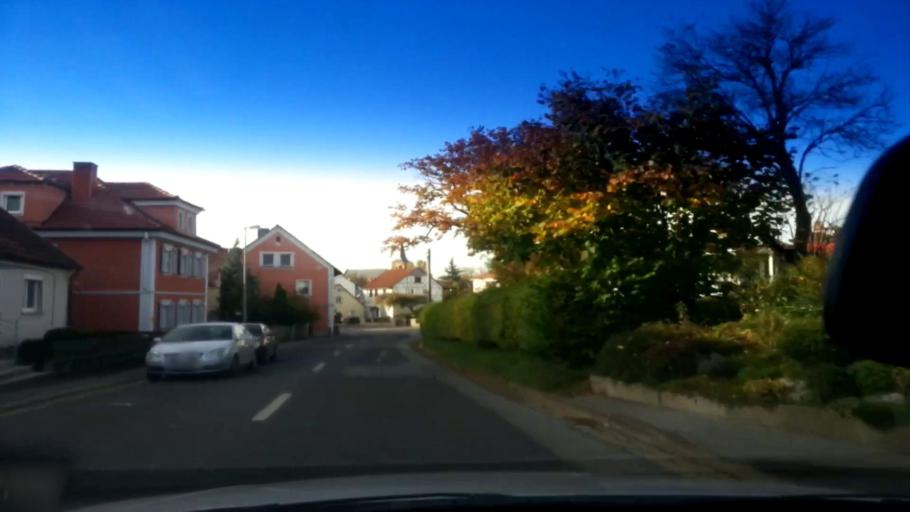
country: DE
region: Bavaria
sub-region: Upper Franconia
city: Schesslitz
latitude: 49.9738
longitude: 11.0390
